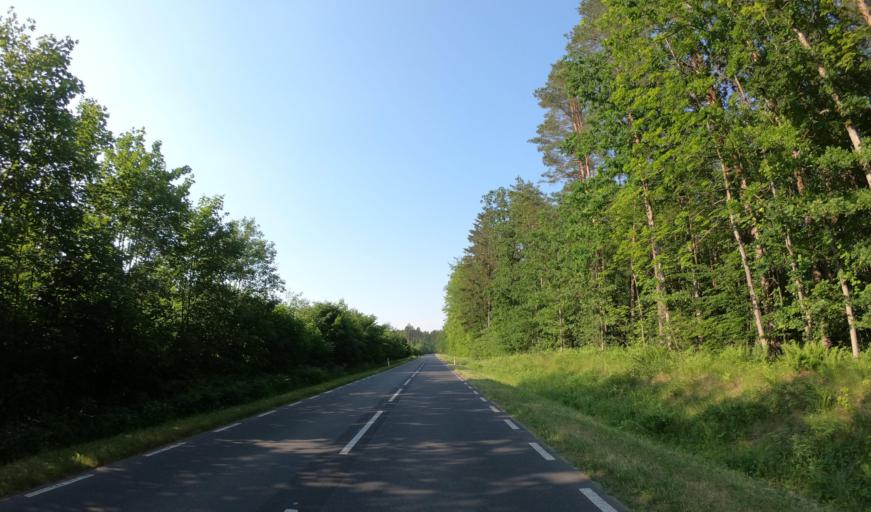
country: PL
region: West Pomeranian Voivodeship
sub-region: Powiat stargardzki
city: Chociwel
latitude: 53.4884
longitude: 15.3396
